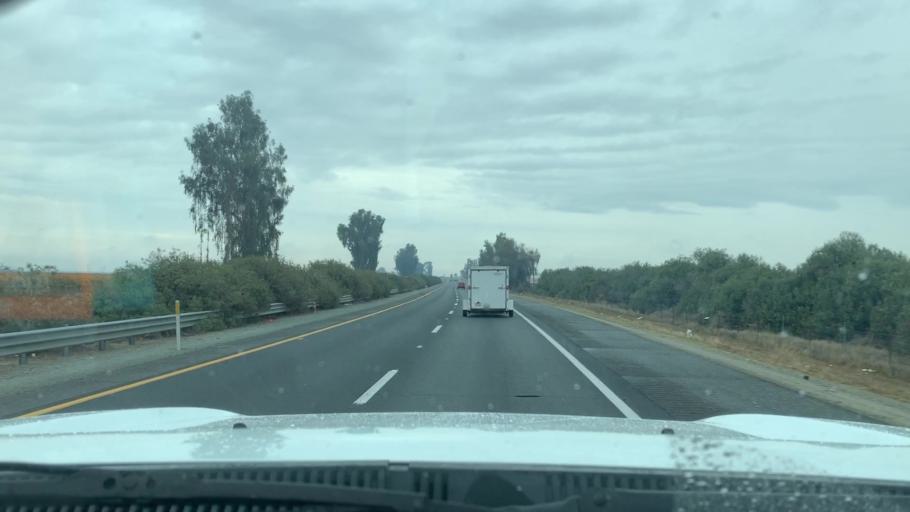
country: US
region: California
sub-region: Kern County
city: Delano
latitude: 35.8265
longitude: -119.2586
